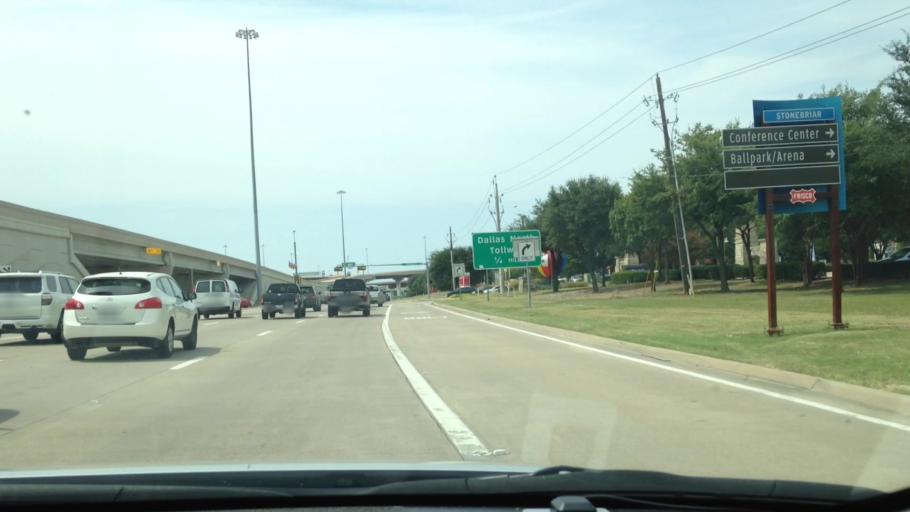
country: US
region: Texas
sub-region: Collin County
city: Frisco
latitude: 33.0943
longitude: -96.8135
